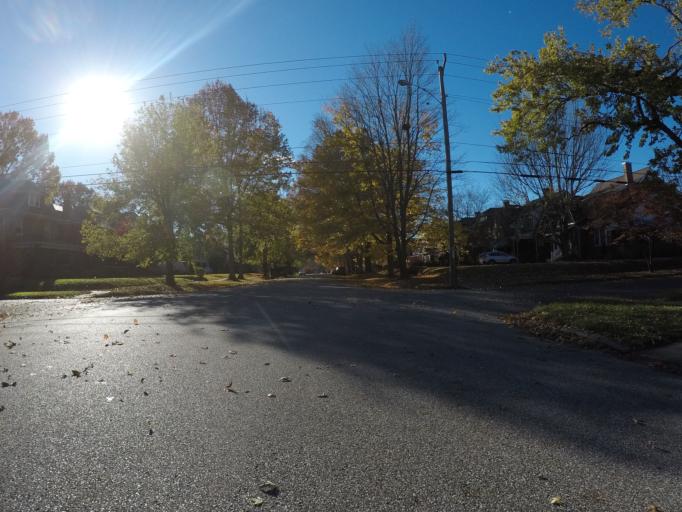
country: US
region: West Virginia
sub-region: Cabell County
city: Huntington
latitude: 38.4096
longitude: -82.4495
